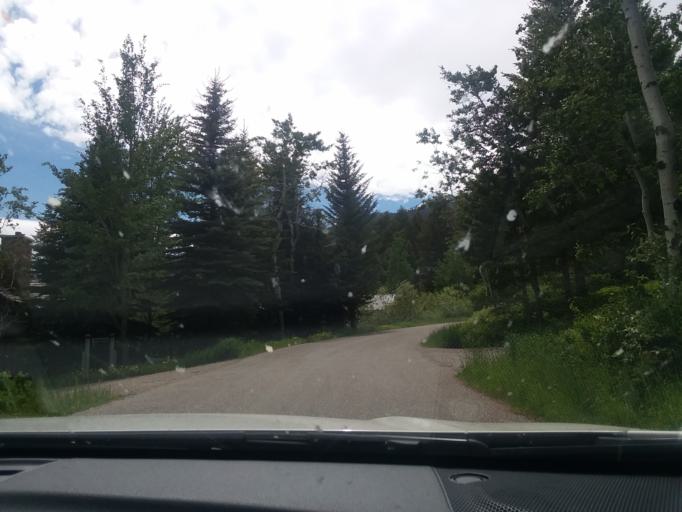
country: US
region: Wyoming
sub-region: Teton County
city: Moose Wilson Road
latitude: 43.5860
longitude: -110.8350
